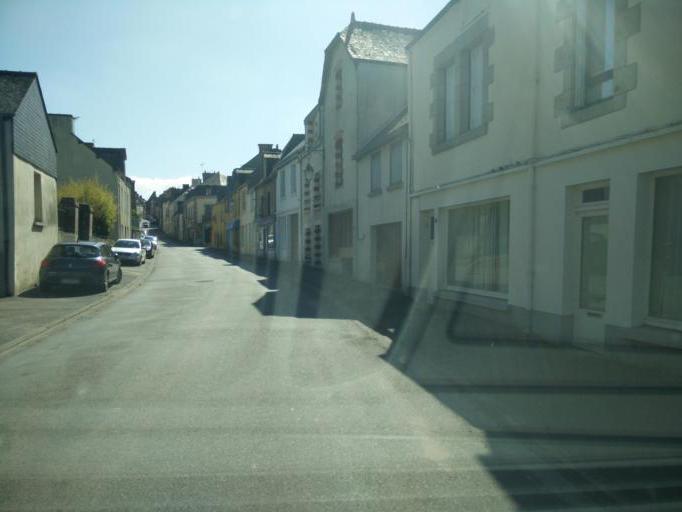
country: FR
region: Brittany
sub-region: Departement du Morbihan
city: Josselin
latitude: 47.9532
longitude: -2.5531
